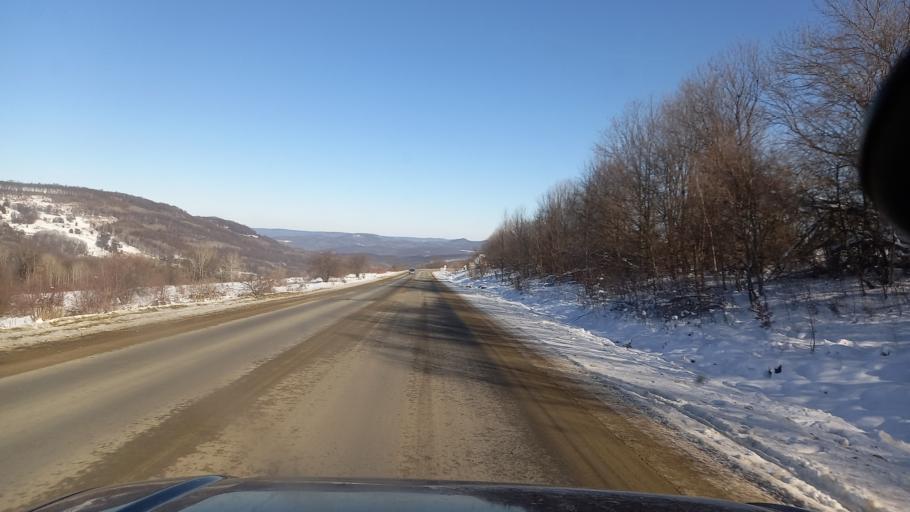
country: RU
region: Adygeya
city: Kamennomostskiy
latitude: 44.2288
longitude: 40.1174
